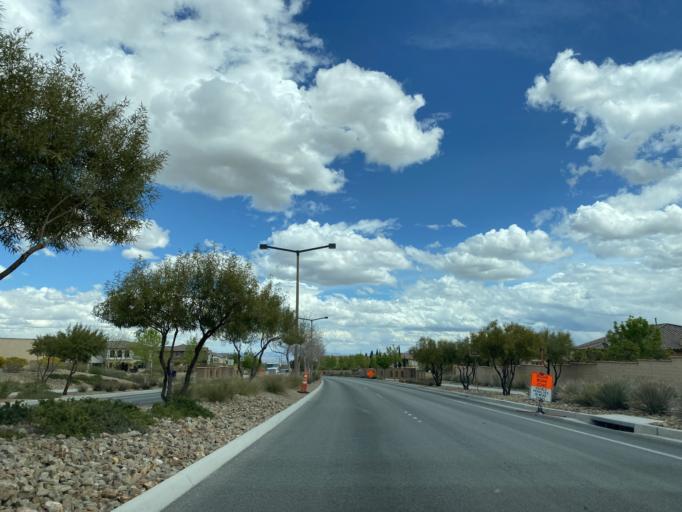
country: US
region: Nevada
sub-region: Clark County
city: Summerlin South
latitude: 36.1700
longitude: -115.3620
